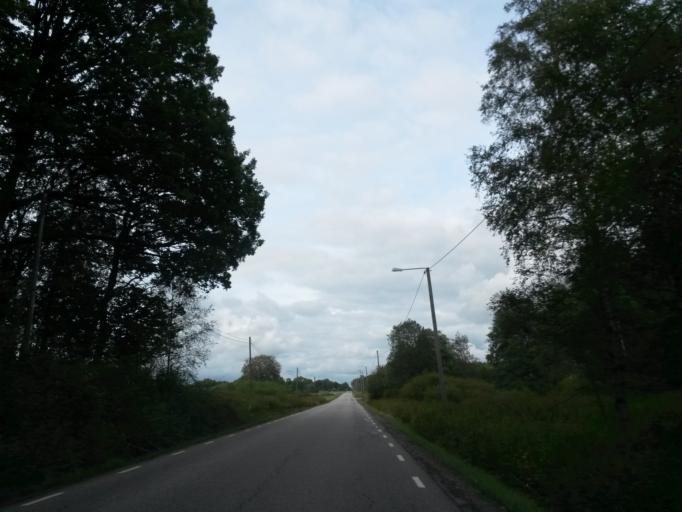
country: SE
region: Vaestra Goetaland
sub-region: Boras Kommun
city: Ganghester
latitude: 57.7451
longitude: 13.0006
